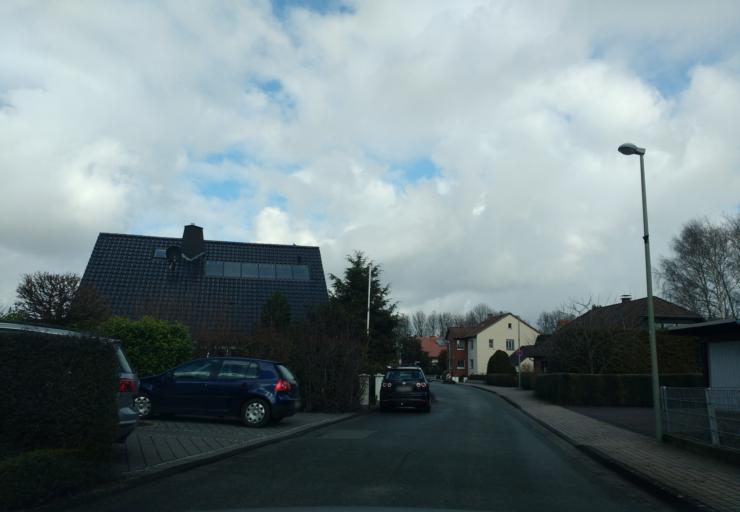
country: DE
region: North Rhine-Westphalia
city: Bad Lippspringe
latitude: 51.7406
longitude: 8.8203
